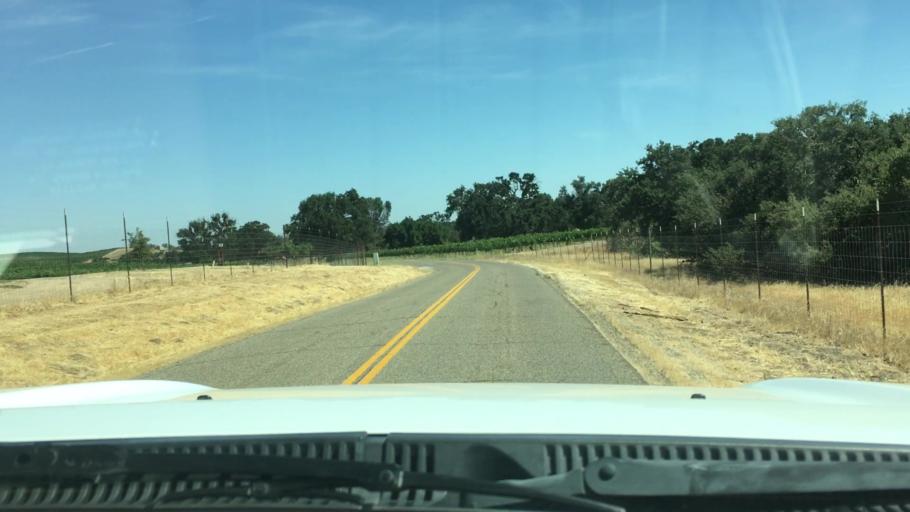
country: US
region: California
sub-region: San Luis Obispo County
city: Templeton
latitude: 35.5686
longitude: -120.6073
